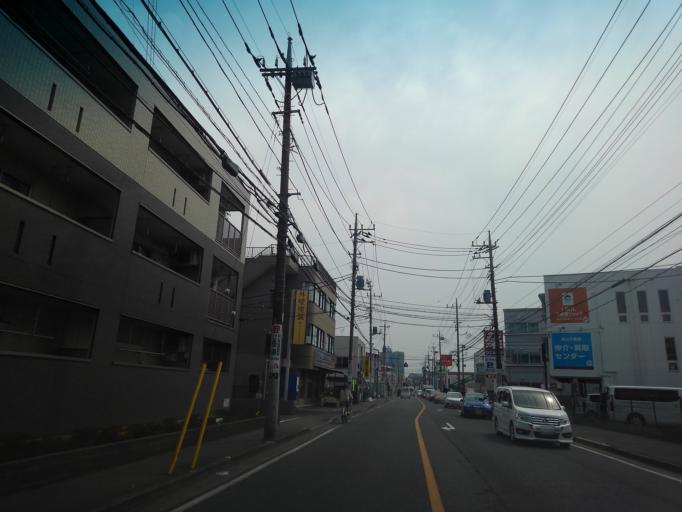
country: JP
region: Saitama
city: Tokorozawa
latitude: 35.8015
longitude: 139.4573
